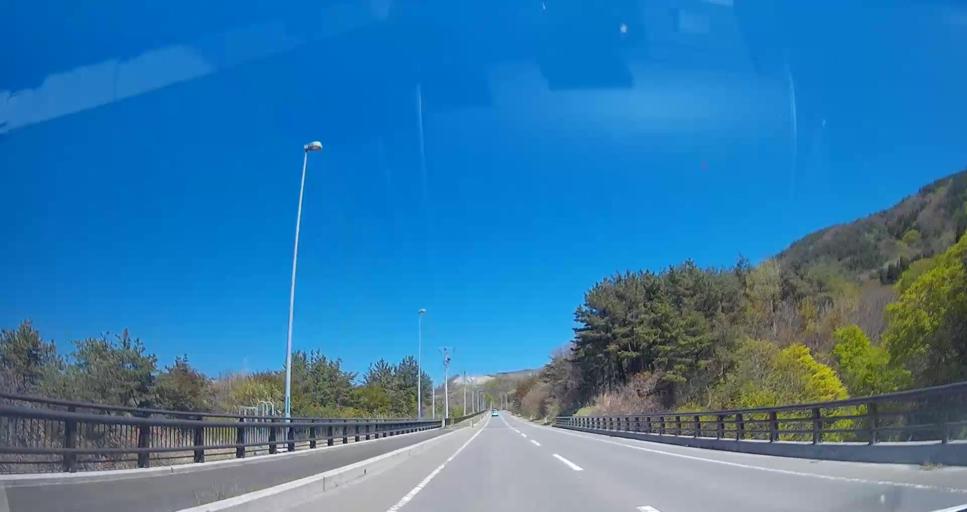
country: JP
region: Aomori
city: Mutsu
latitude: 41.3924
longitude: 141.4174
